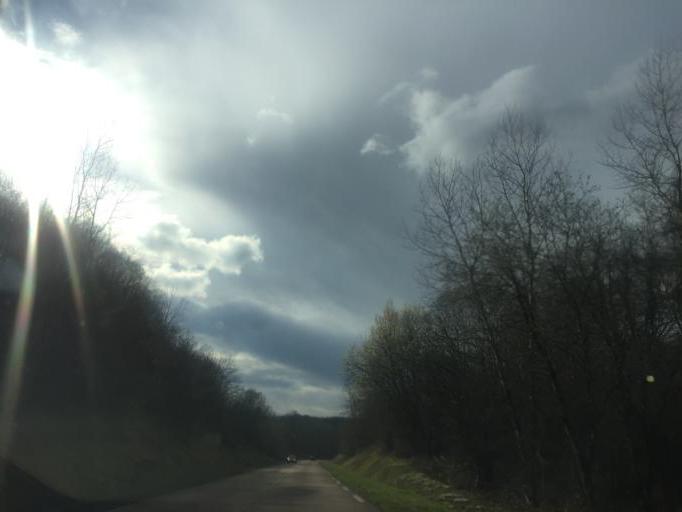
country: FR
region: Bourgogne
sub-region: Departement de la Nievre
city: Clamecy
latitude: 47.4516
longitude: 3.6836
